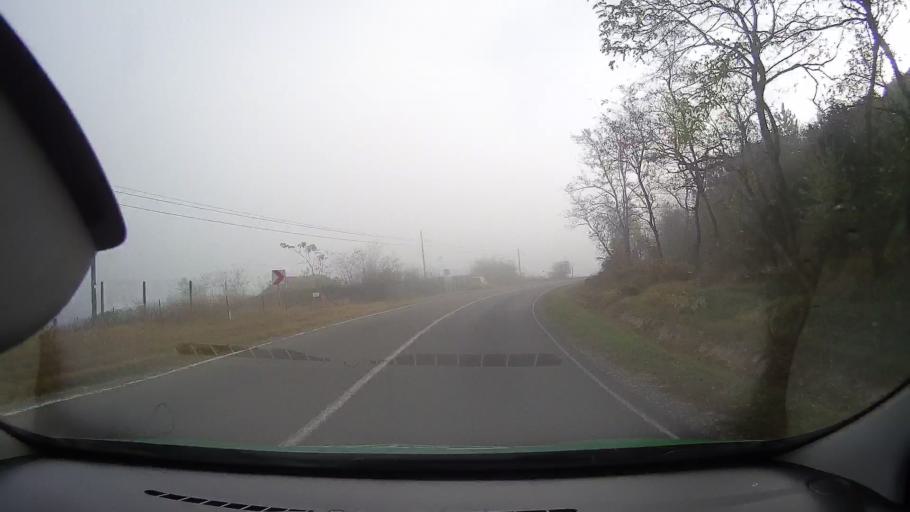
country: RO
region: Tulcea
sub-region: Municipiul Tulcea
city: Tulcea
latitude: 45.1676
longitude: 28.8362
